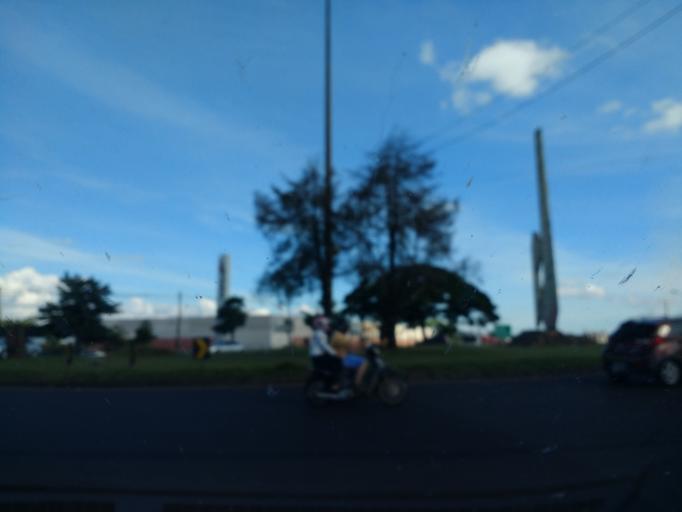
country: BR
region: Parana
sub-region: Maringa
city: Maringa
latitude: -23.4184
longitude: -51.9718
